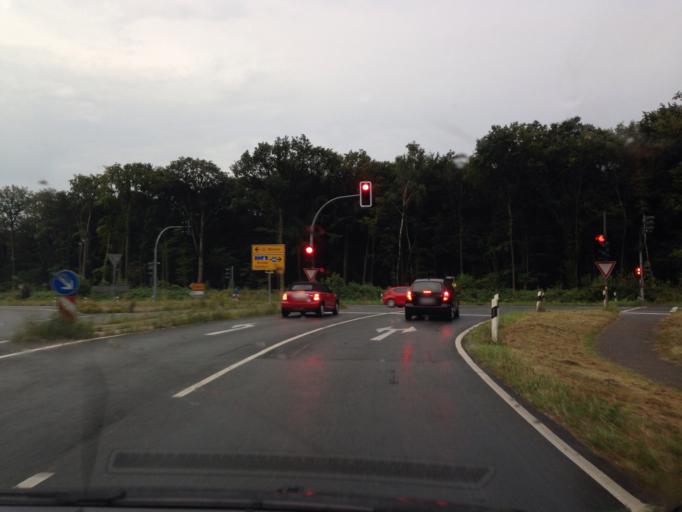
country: DE
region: North Rhine-Westphalia
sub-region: Regierungsbezirk Munster
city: Muenster
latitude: 51.9885
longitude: 7.5807
